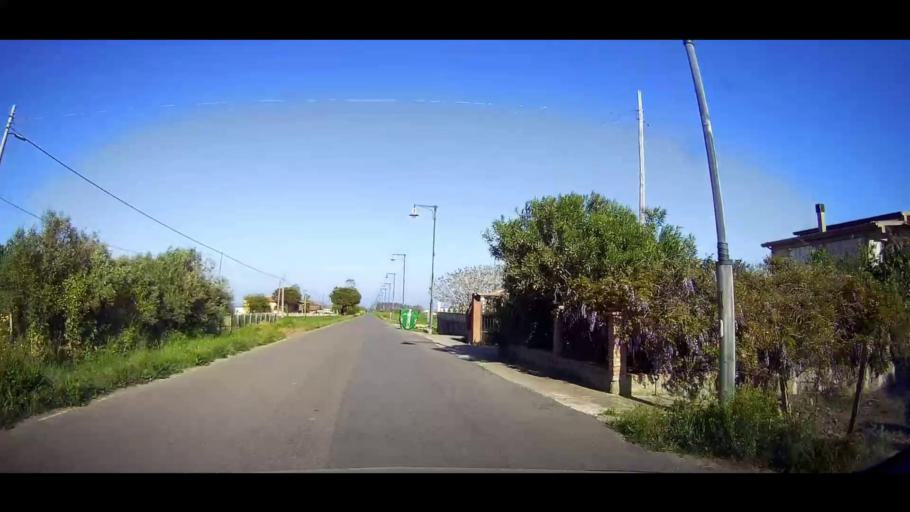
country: IT
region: Calabria
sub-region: Provincia di Crotone
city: Crotone
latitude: 39.0249
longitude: 17.1775
